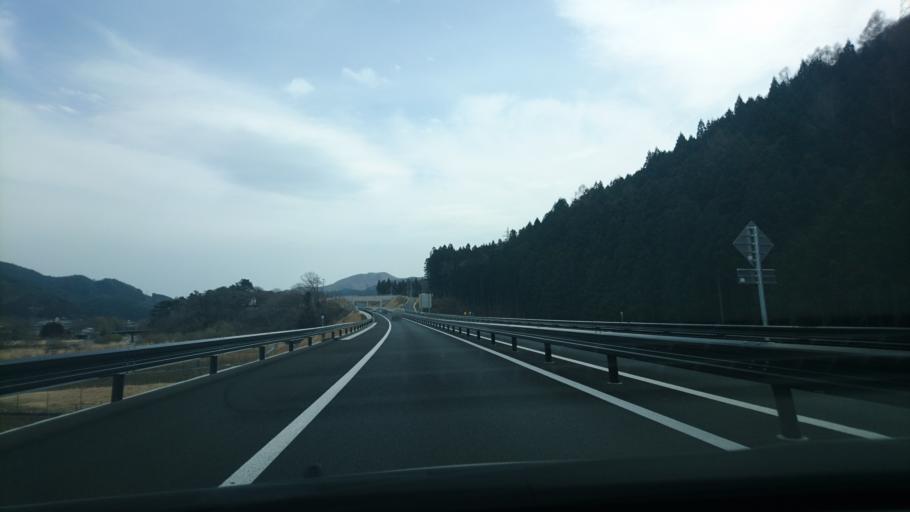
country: JP
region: Iwate
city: Kamaishi
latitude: 39.2513
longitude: 141.7844
